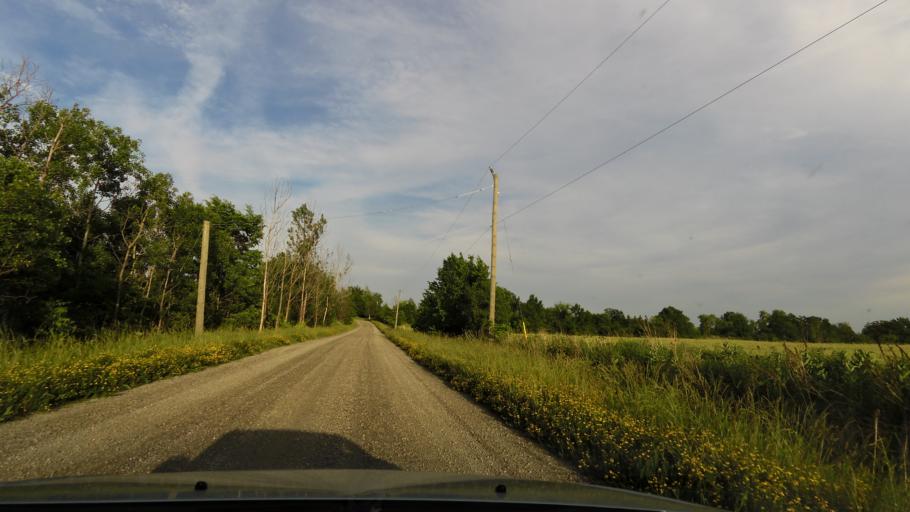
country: CA
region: Ontario
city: Ancaster
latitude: 43.0704
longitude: -79.9676
